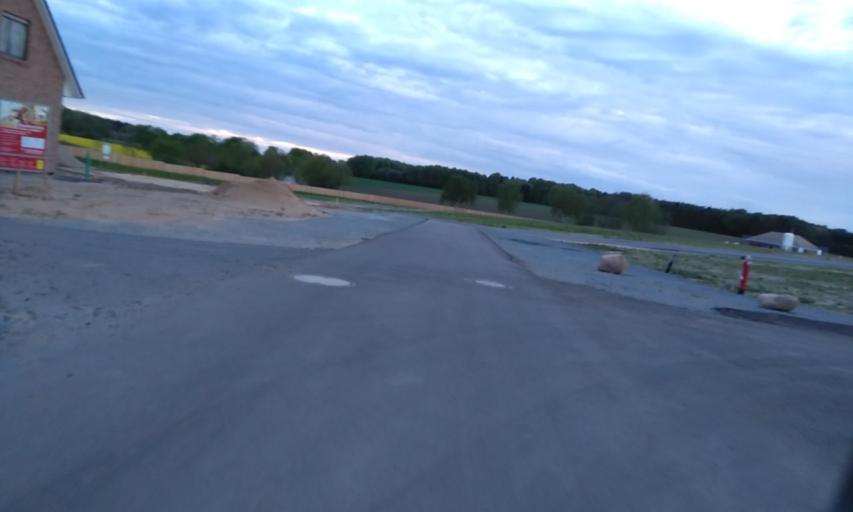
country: DE
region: Lower Saxony
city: Horneburg
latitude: 53.5080
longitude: 9.5626
